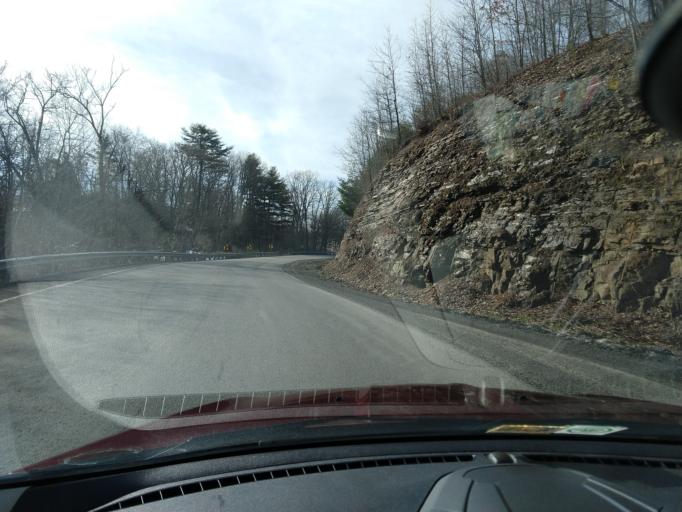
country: US
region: West Virginia
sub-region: Pocahontas County
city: Marlinton
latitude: 38.2108
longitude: -80.1045
